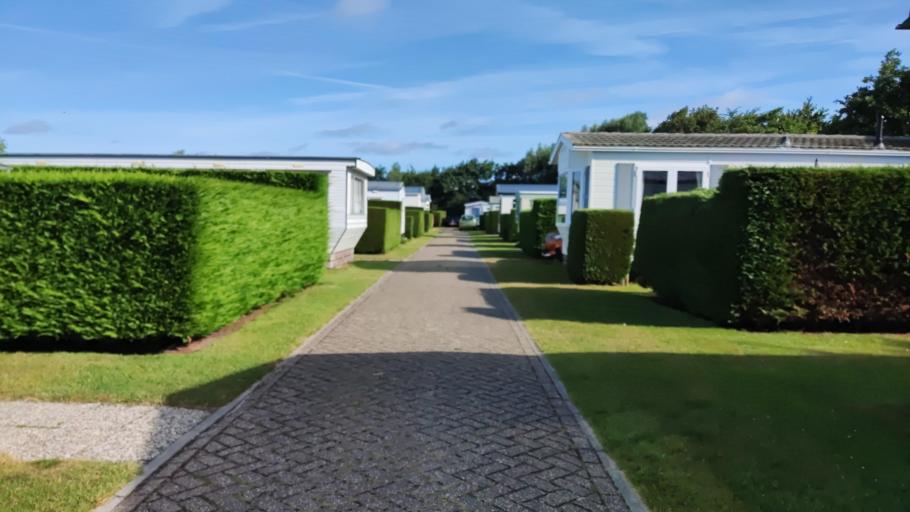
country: NL
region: North Holland
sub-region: Gemeente Texel
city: Den Burg
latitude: 53.0970
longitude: 4.7682
